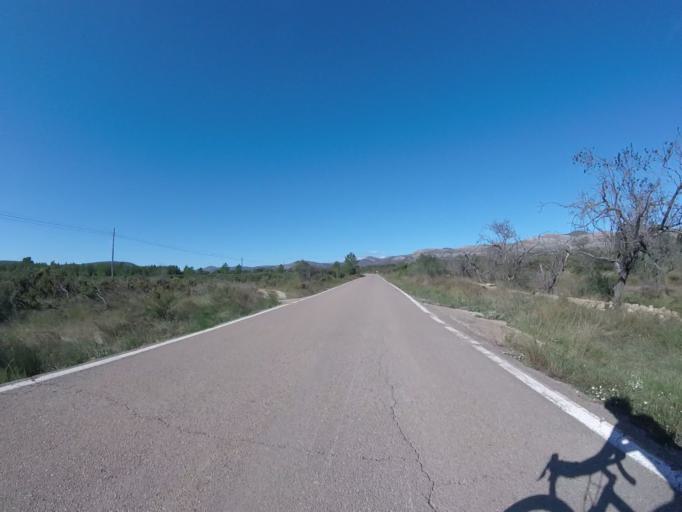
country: ES
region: Valencia
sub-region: Provincia de Castello
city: Chert/Xert
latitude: 40.4558
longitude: 0.1410
